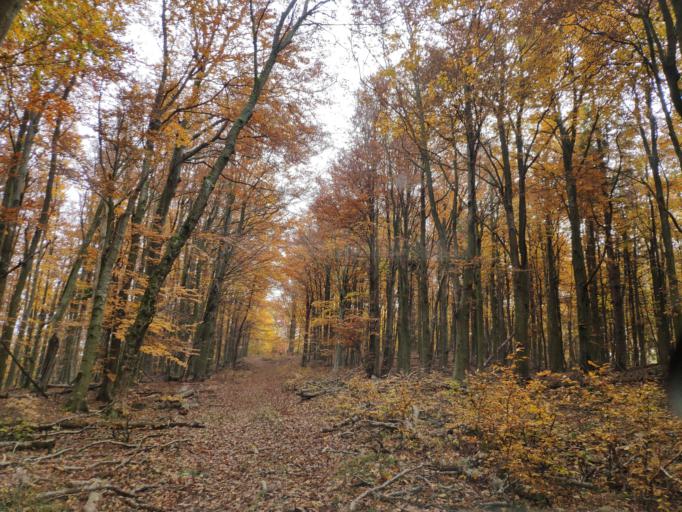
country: SK
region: Kosicky
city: Medzev
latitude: 48.7353
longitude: 21.0039
